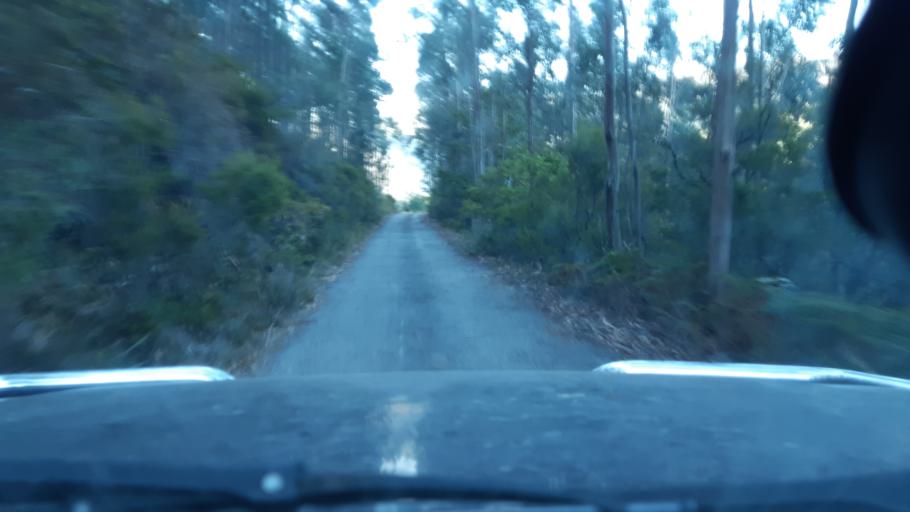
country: PT
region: Viseu
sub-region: Mortagua
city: Mortagua
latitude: 40.5219
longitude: -8.2524
